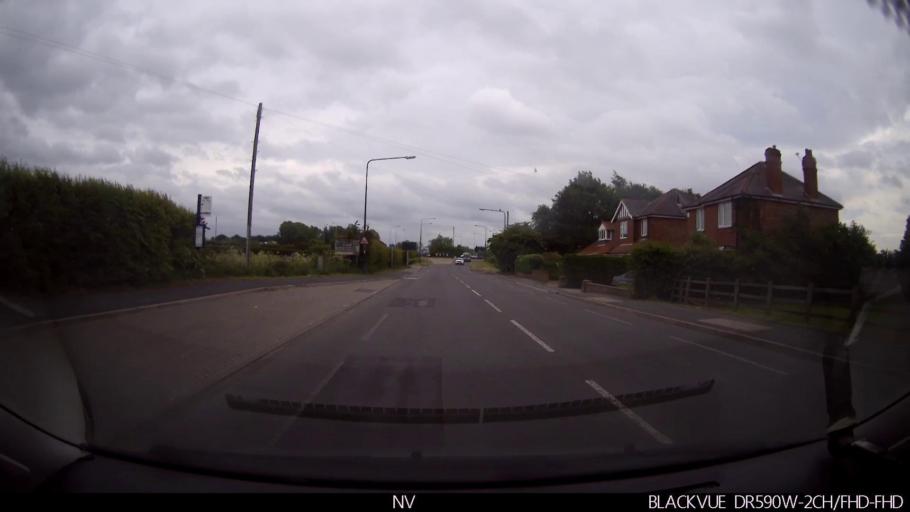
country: GB
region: England
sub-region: City of York
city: Haxby
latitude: 54.0026
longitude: -1.0731
